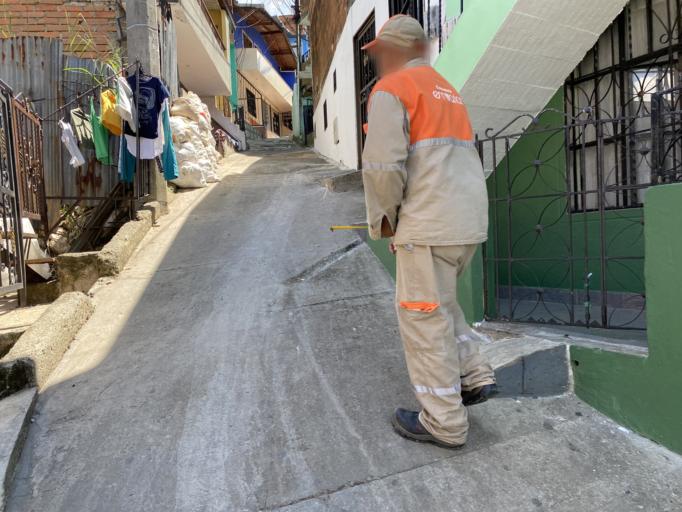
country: CO
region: Antioquia
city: Bello
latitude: 6.2951
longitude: -75.5506
